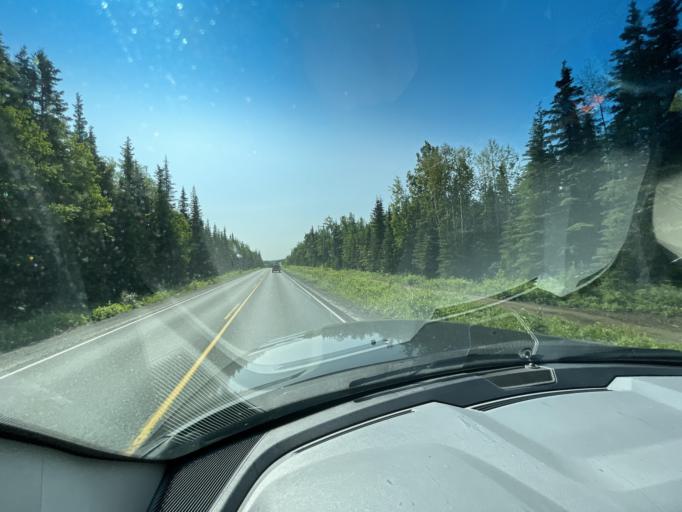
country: US
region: Alaska
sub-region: Kenai Peninsula Borough
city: Cohoe
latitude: 60.3056
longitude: -151.2874
